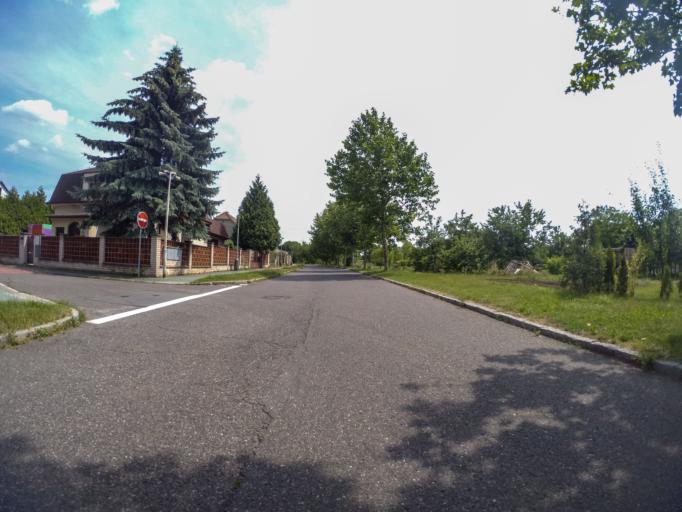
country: CZ
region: Praha
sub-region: Praha 19
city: Kbely
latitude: 50.1296
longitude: 14.5553
